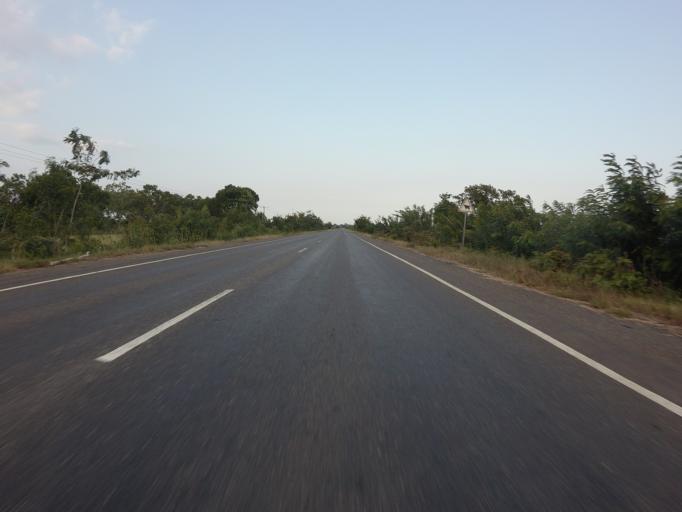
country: GH
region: Volta
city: Anloga
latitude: 6.0779
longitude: 0.5913
